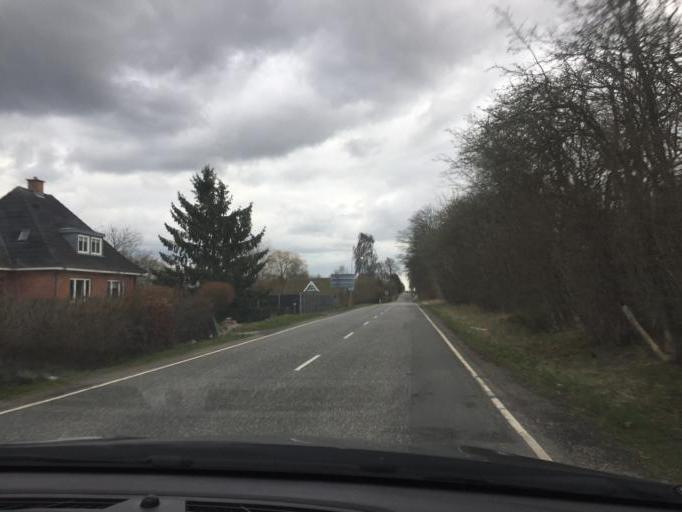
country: DK
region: South Denmark
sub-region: Kerteminde Kommune
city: Langeskov
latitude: 55.3049
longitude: 10.5905
